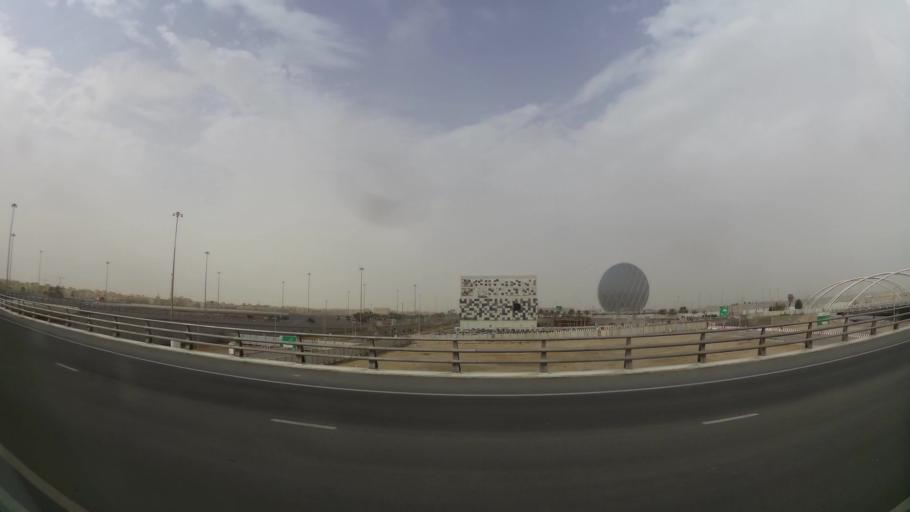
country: AE
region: Abu Dhabi
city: Abu Dhabi
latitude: 24.4423
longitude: 54.5857
